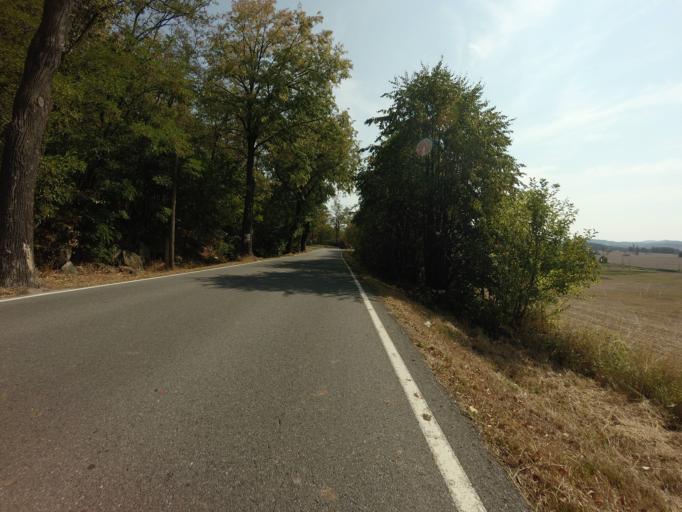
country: CZ
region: Central Bohemia
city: Sedlcany
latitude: 49.6183
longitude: 14.4022
